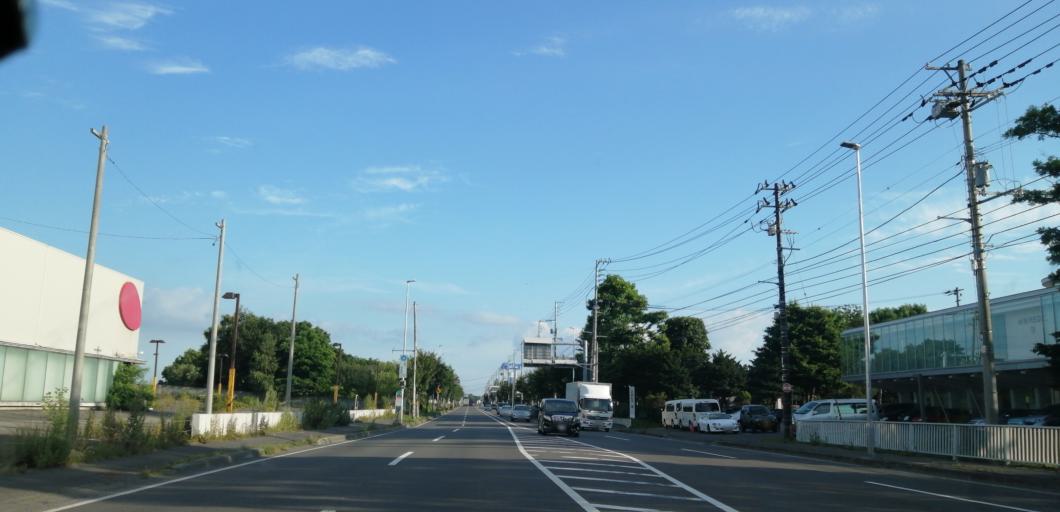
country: JP
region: Hokkaido
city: Kitahiroshima
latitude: 42.9971
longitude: 141.5621
